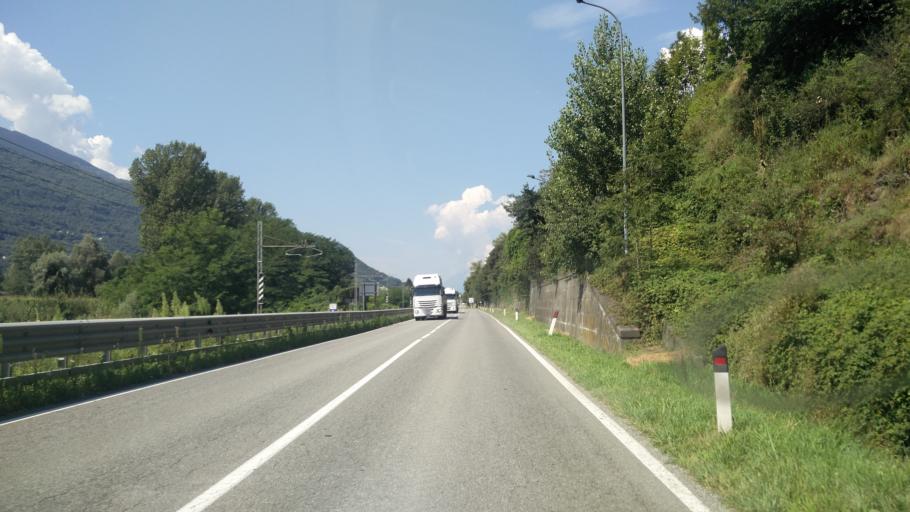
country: IT
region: Lombardy
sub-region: Provincia di Sondrio
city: San Giacomo
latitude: 46.1586
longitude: 10.0433
